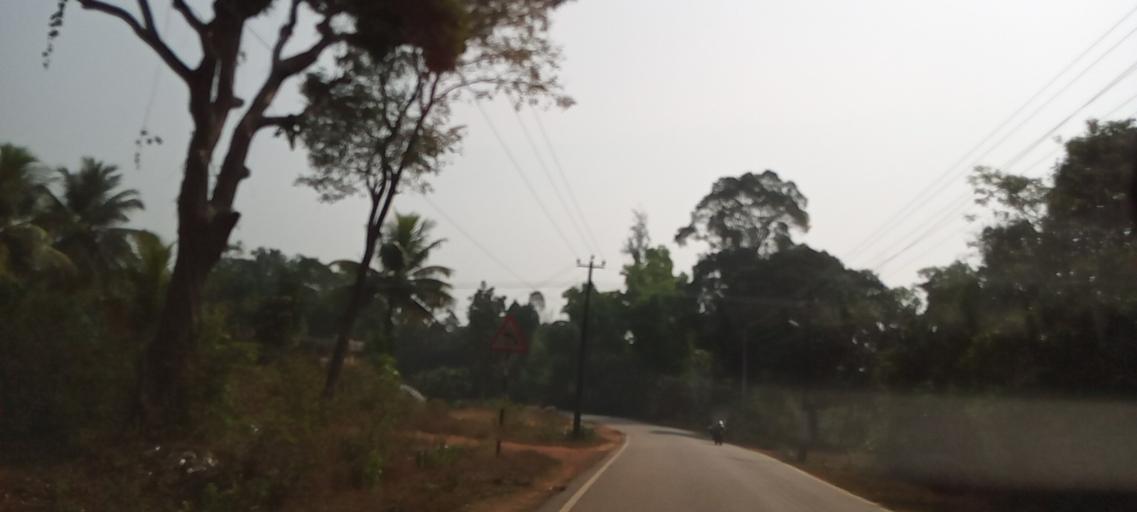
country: IN
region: Karnataka
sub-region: Udupi
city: Manipala
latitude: 13.5114
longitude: 74.8245
